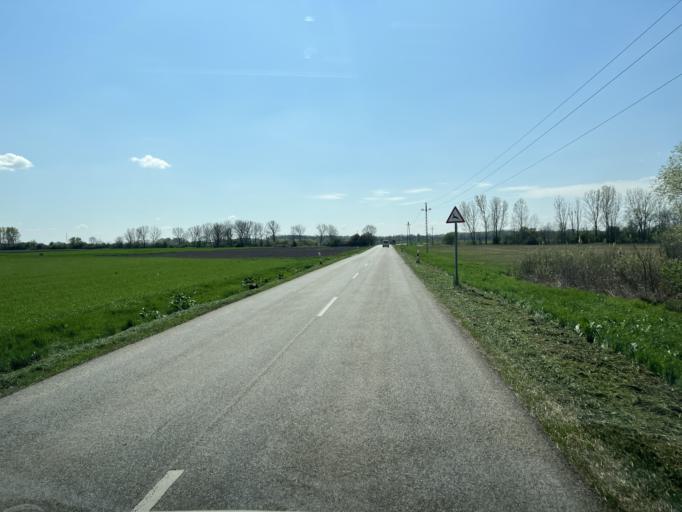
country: HU
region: Pest
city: Inarcs
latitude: 47.2305
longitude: 19.3055
